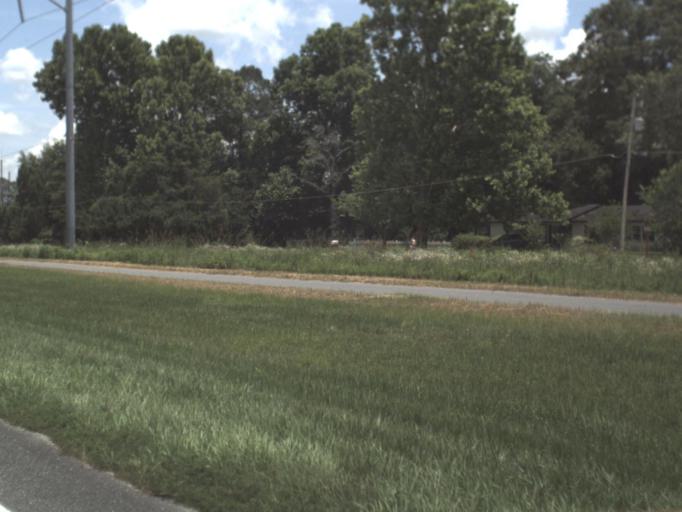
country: US
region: Florida
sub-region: Alachua County
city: Archer
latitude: 29.5648
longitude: -82.4772
